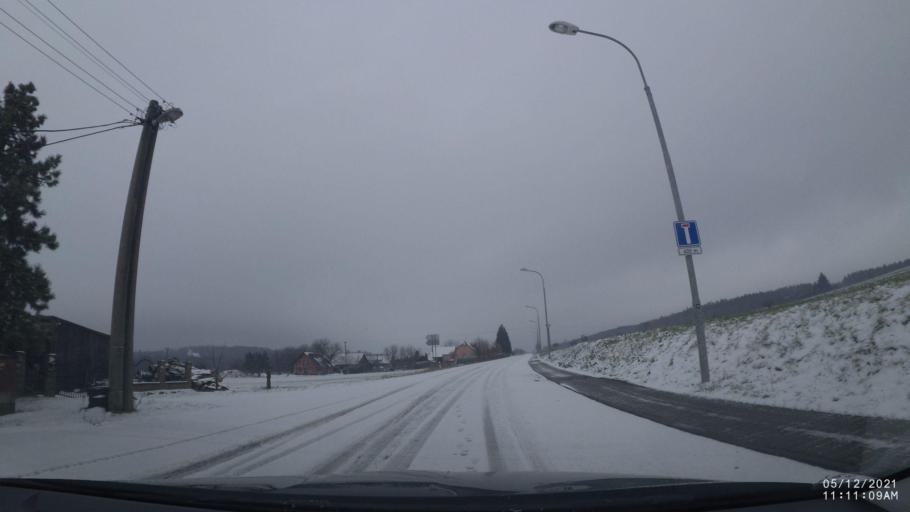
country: CZ
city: Solnice
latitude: 50.1816
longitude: 16.2229
